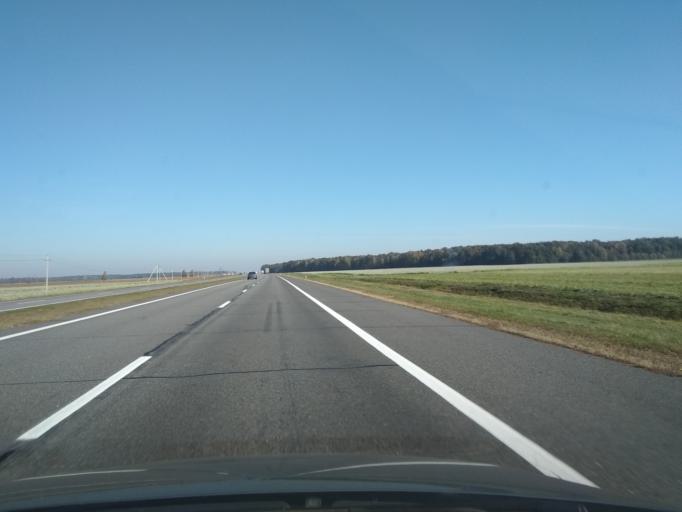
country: BY
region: Brest
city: Antopal'
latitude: 52.3905
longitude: 24.7771
